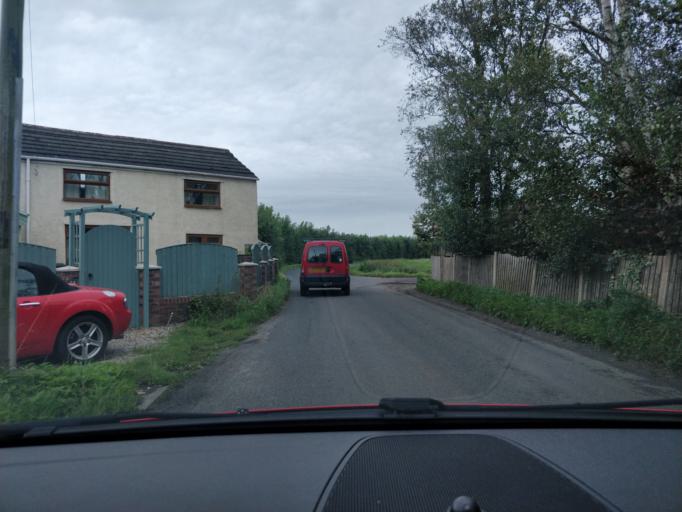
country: GB
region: England
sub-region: Lancashire
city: Ormskirk
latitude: 53.6132
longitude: -2.8624
